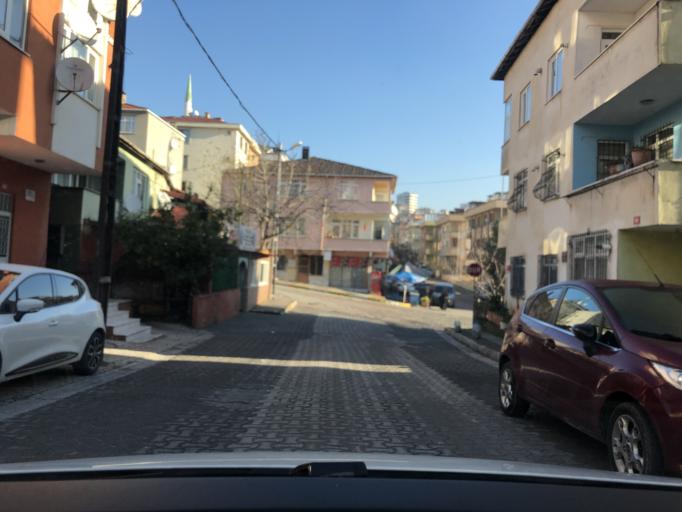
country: TR
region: Istanbul
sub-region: Atasehir
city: Atasehir
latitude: 40.9751
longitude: 29.1245
